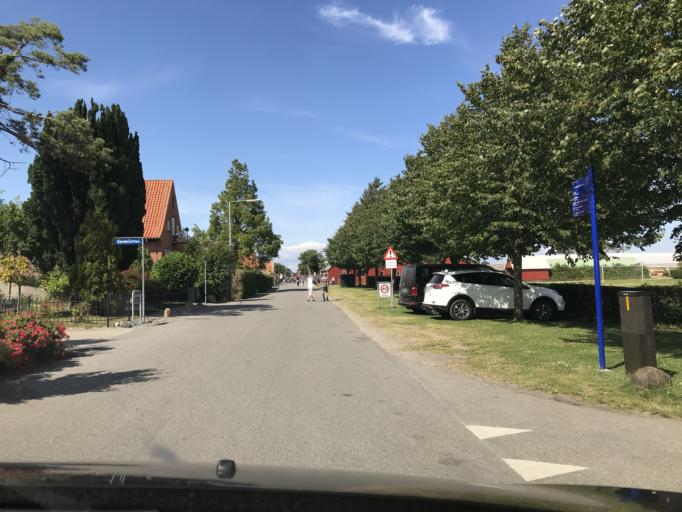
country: DK
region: South Denmark
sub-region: AEro Kommune
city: Marstal
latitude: 54.8495
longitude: 10.5214
